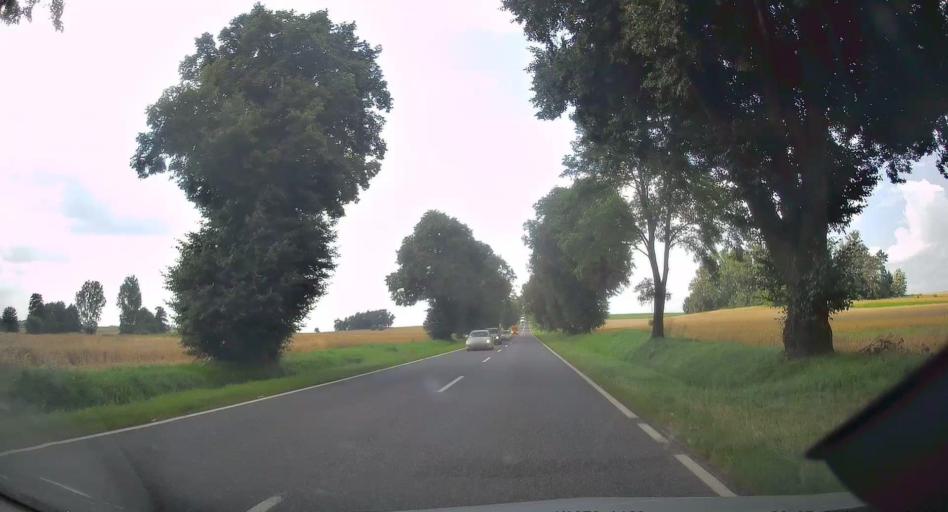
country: PL
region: Lodz Voivodeship
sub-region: Powiat skierniewicki
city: Gluchow
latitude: 51.7838
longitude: 20.0566
